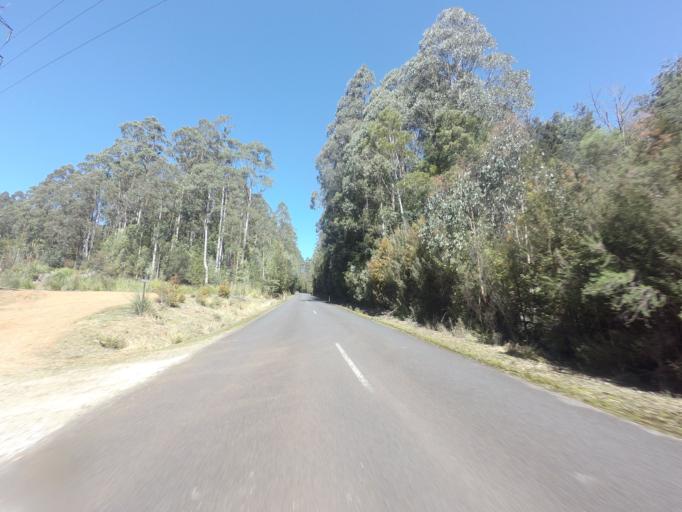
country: AU
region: Tasmania
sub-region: Huon Valley
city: Geeveston
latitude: -42.8234
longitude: 146.3140
